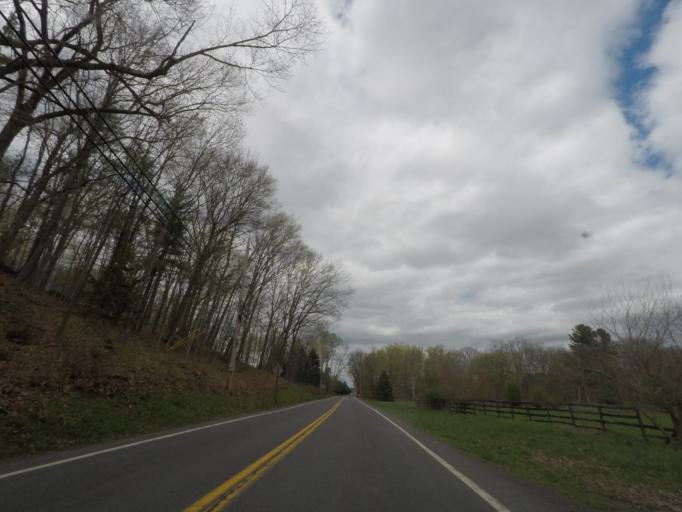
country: US
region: New York
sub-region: Columbia County
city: Philmont
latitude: 42.3009
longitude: -73.6351
